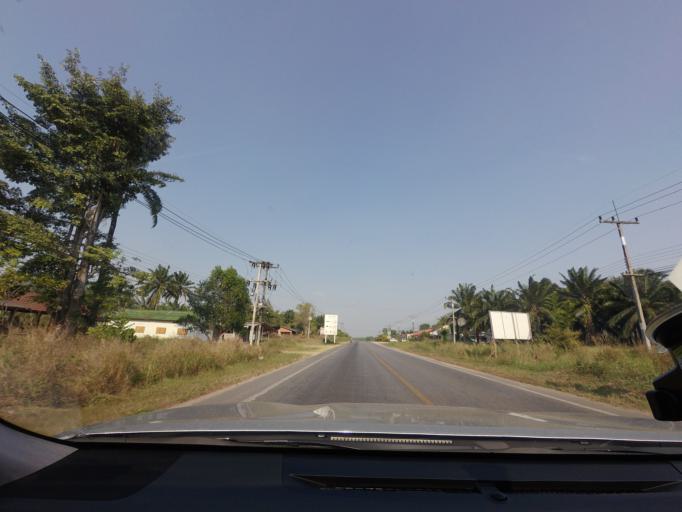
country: TH
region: Surat Thani
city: Chai Buri
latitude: 8.5697
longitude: 99.1198
